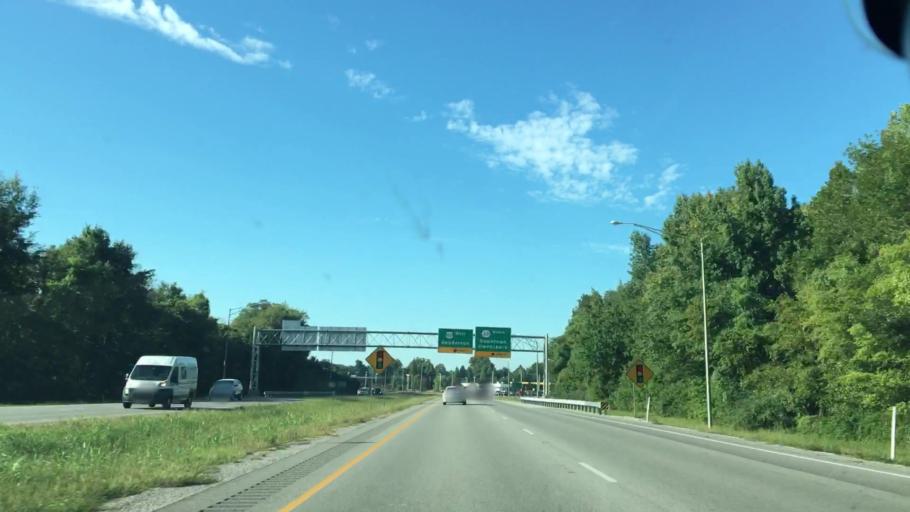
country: US
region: Kentucky
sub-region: Daviess County
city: Owensboro
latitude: 37.7717
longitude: -87.1652
